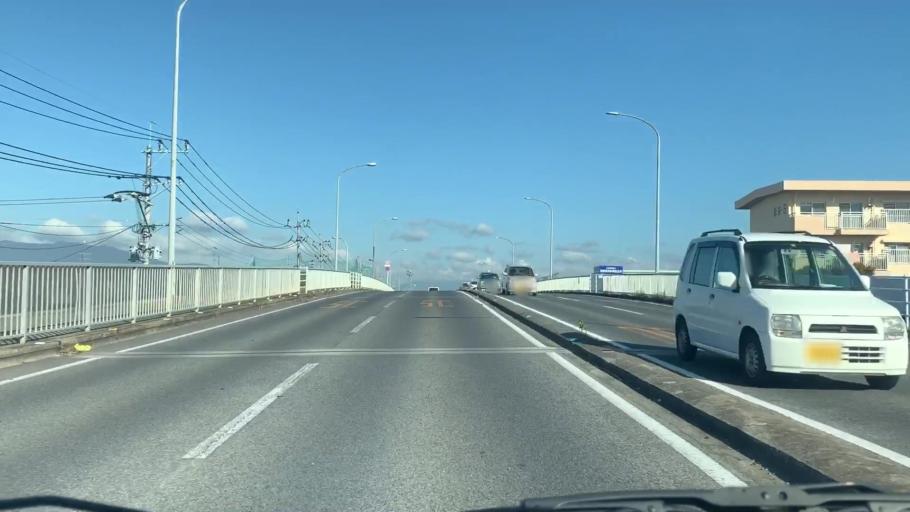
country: JP
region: Saga Prefecture
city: Saga-shi
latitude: 33.2587
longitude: 130.2732
